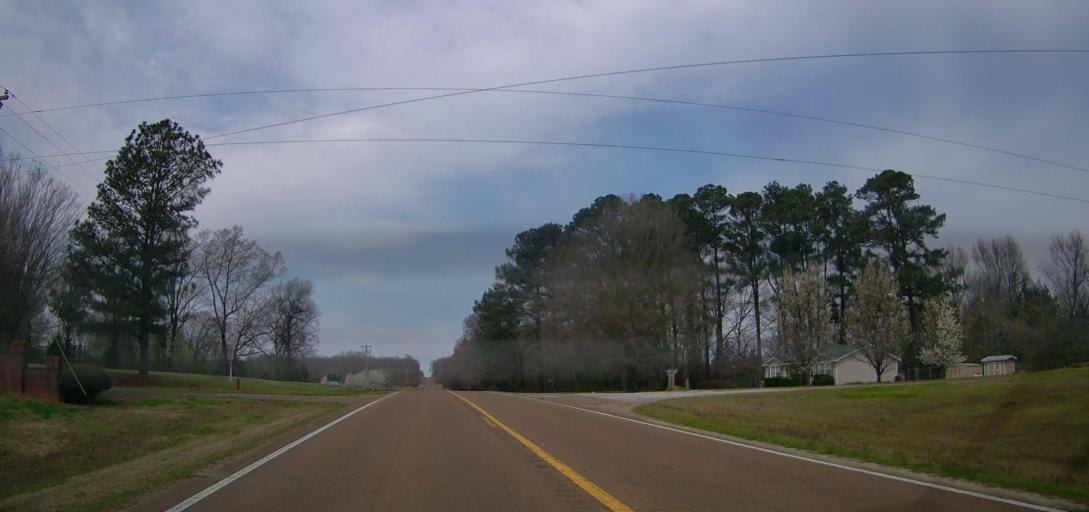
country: US
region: Mississippi
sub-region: Marshall County
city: Byhalia
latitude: 34.8326
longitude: -89.5778
